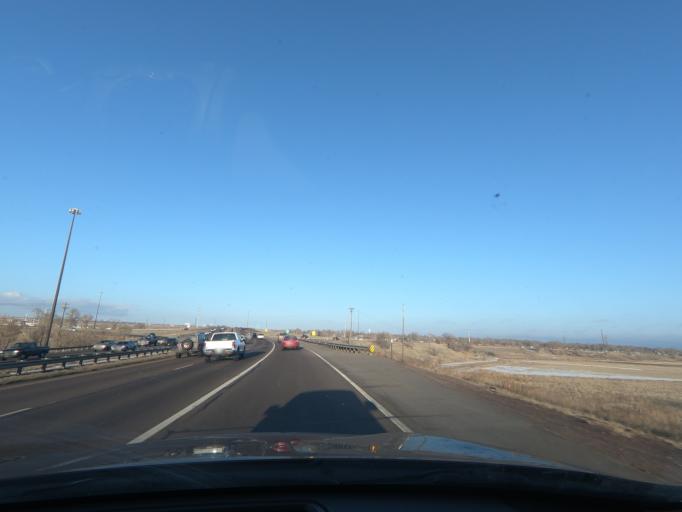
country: US
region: Colorado
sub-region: El Paso County
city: Stratmoor
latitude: 38.7657
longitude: -104.7645
